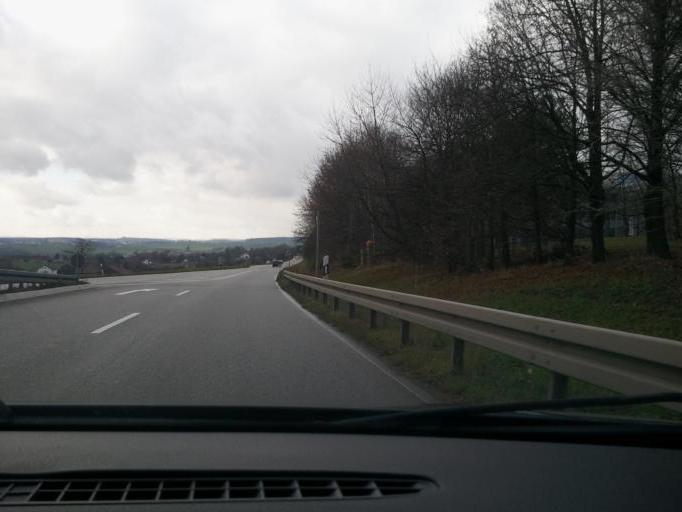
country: DE
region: Baden-Wuerttemberg
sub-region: Regierungsbezirk Stuttgart
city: Schwieberdingen
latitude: 48.8813
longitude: 9.0965
